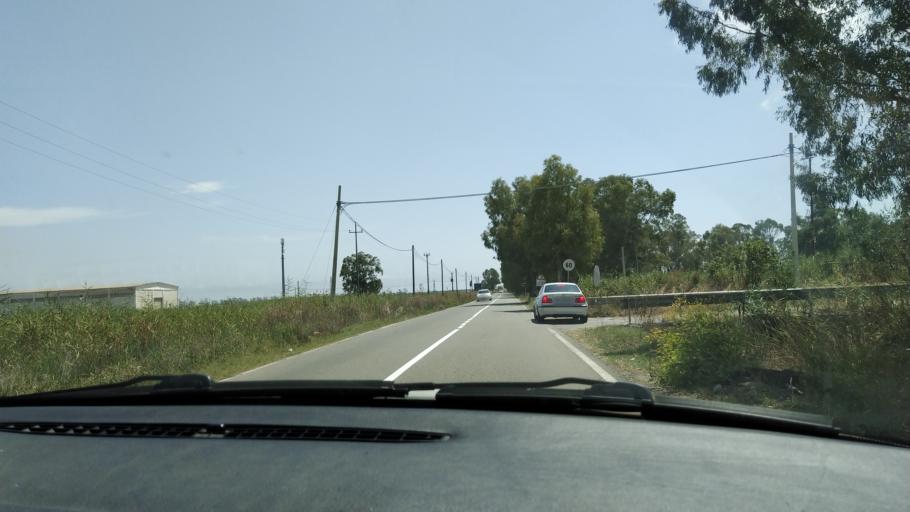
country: IT
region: Basilicate
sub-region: Provincia di Matera
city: Marconia
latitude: 40.3396
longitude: 16.7646
